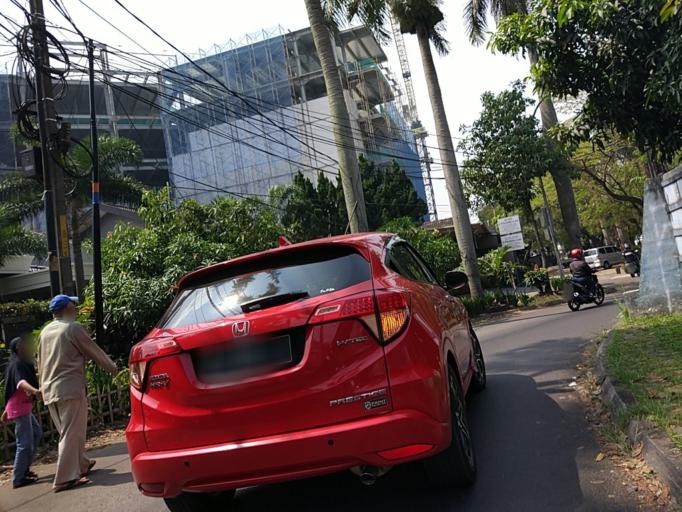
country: ID
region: West Java
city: Margahayukencana
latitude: -6.9325
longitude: 107.5754
